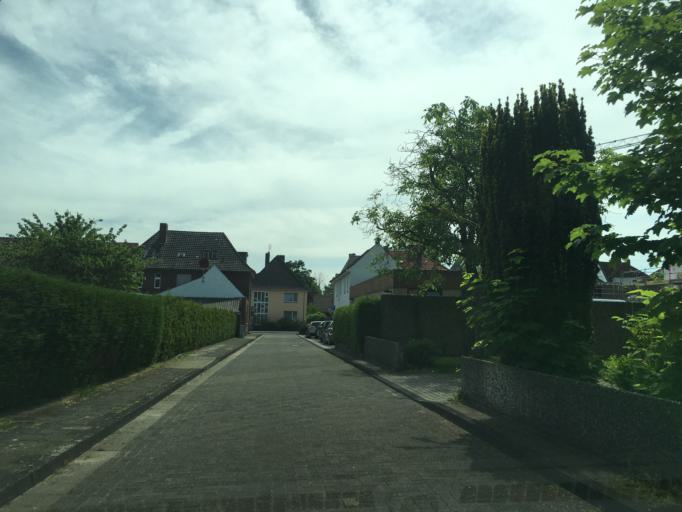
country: DE
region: North Rhine-Westphalia
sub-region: Regierungsbezirk Munster
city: Steinfurt
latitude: 52.1497
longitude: 7.3324
